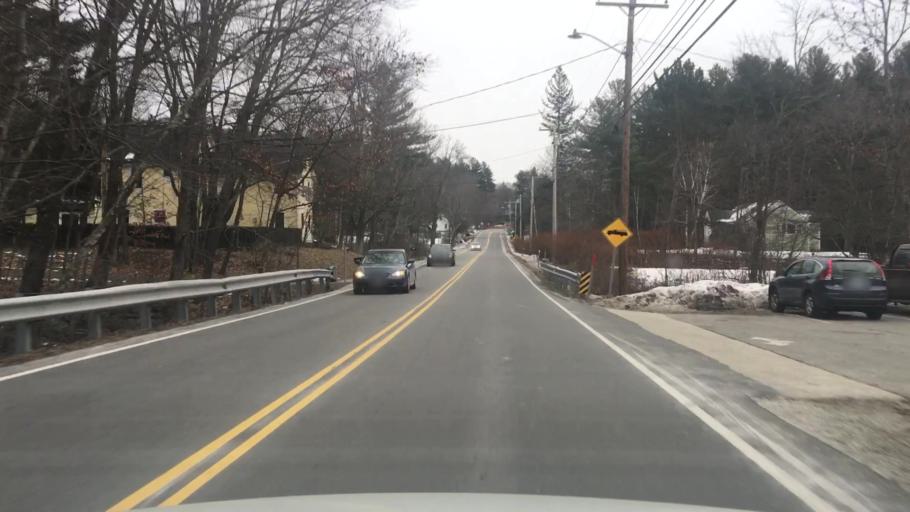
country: US
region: New Hampshire
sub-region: Merrimack County
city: Hopkinton
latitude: 43.1895
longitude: -71.6662
